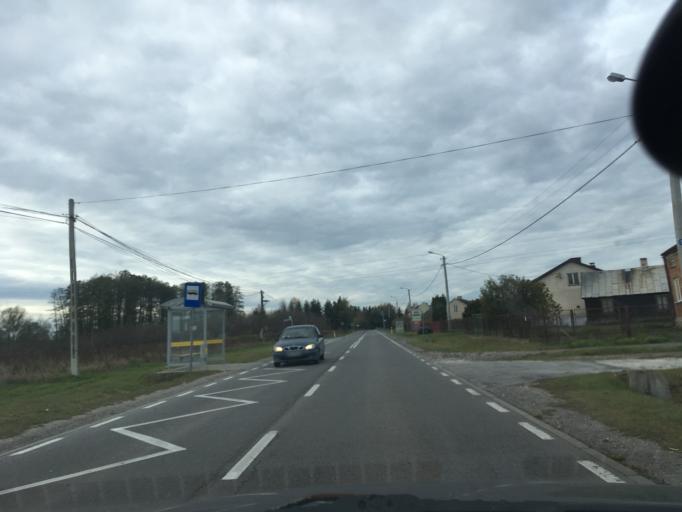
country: PL
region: Masovian Voivodeship
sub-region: Powiat piaseczynski
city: Tarczyn
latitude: 51.9789
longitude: 20.8561
